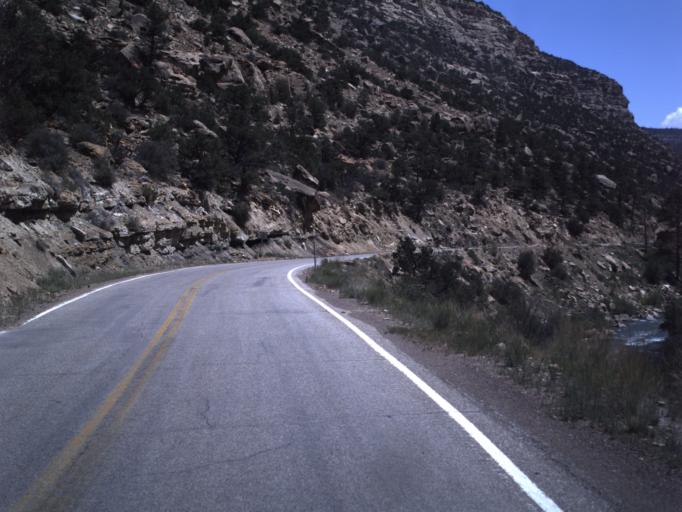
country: US
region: Utah
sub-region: Emery County
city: Orangeville
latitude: 39.2870
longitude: -111.2403
